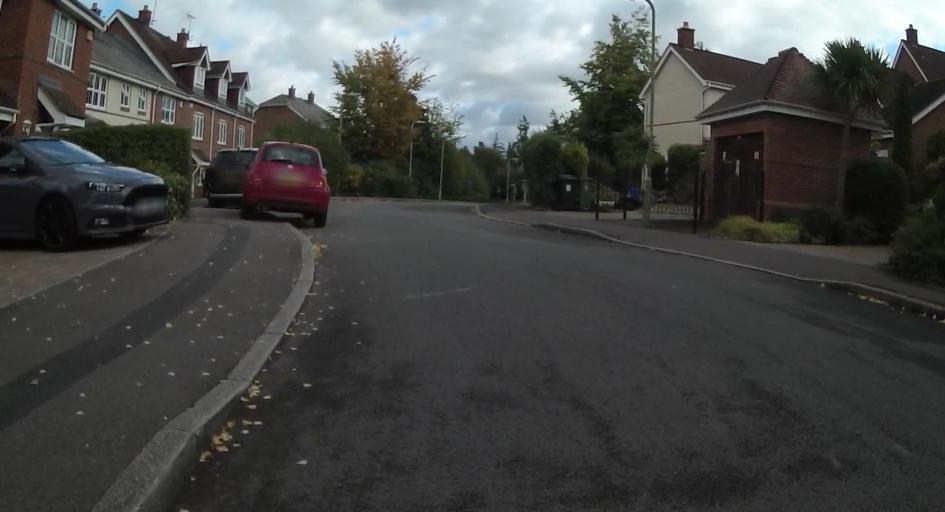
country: GB
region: England
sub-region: Hampshire
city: Fleet
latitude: 51.2929
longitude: -0.8649
